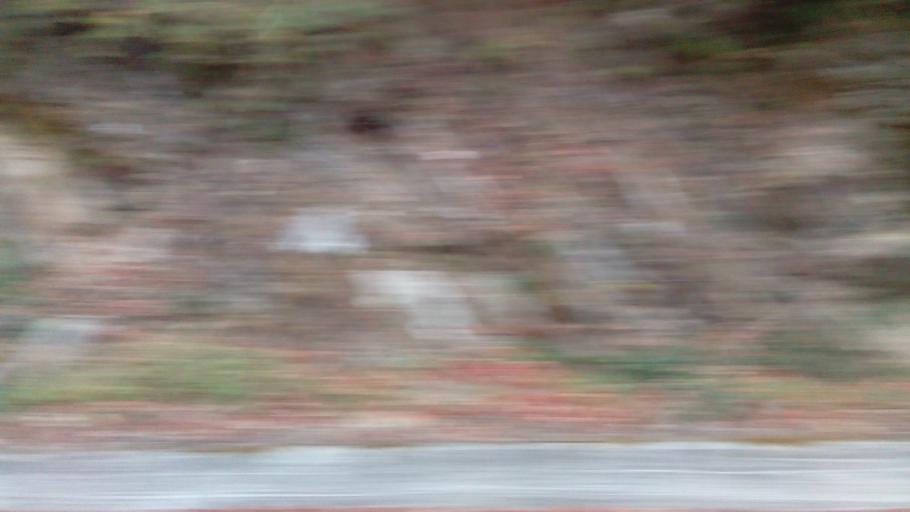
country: TW
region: Taiwan
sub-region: Hualien
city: Hualian
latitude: 24.3722
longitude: 121.3397
